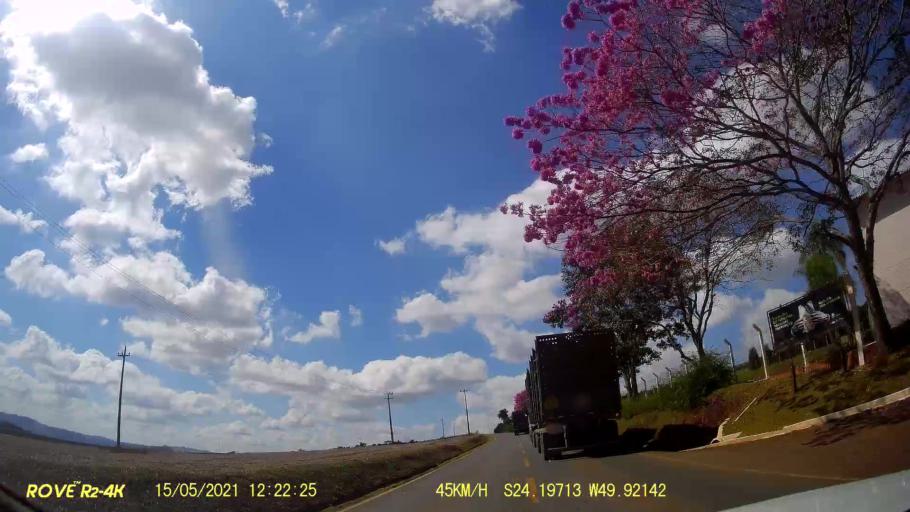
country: BR
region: Parana
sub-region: Jaguariaiva
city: Jaguariaiva
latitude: -24.1971
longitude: -49.9213
